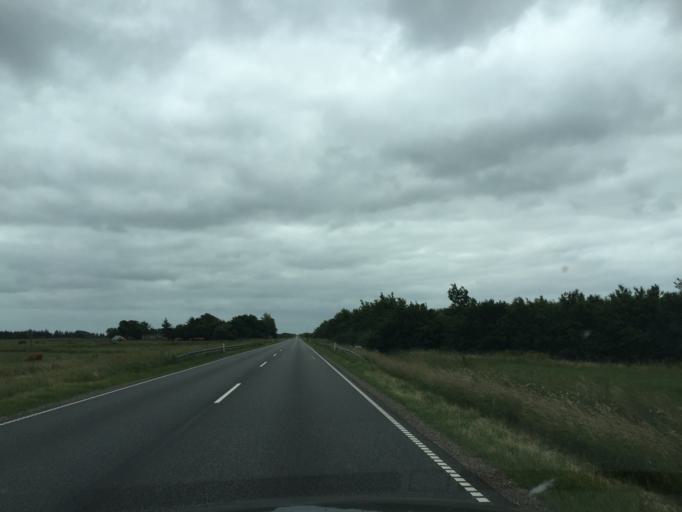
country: DK
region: South Denmark
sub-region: Esbjerg Kommune
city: Ribe
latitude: 55.2533
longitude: 8.7228
